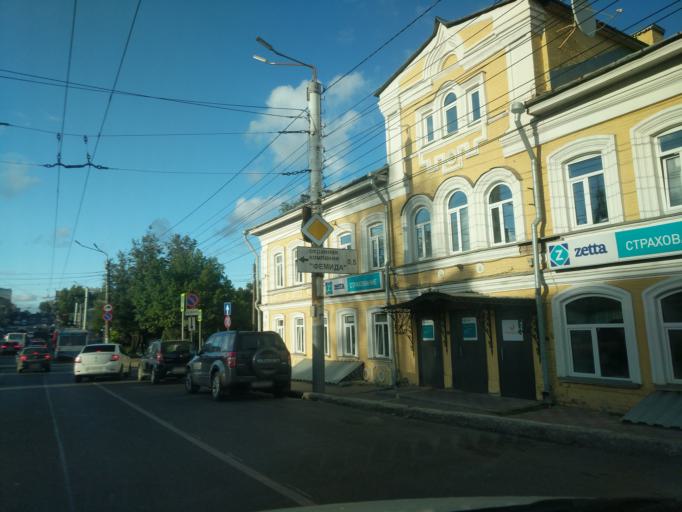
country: RU
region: Kirov
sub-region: Kirovo-Chepetskiy Rayon
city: Kirov
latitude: 58.5993
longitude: 49.6814
